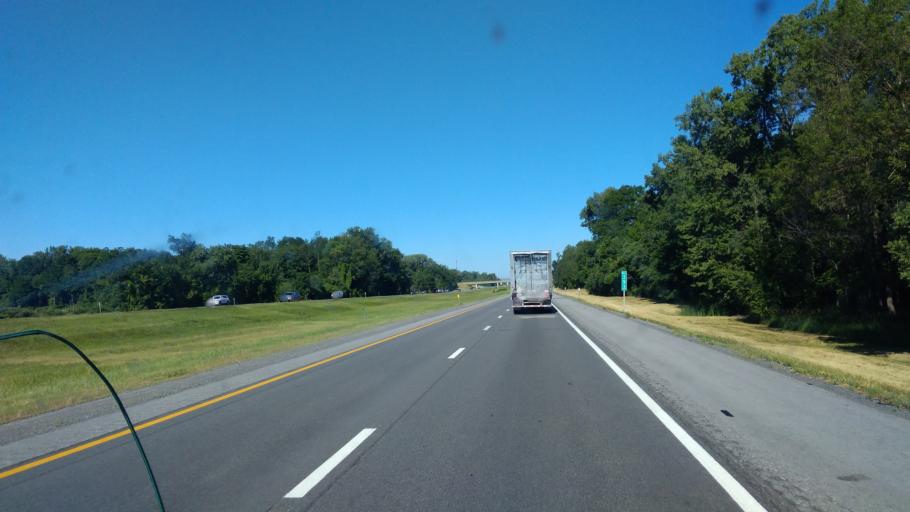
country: US
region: New York
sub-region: Genesee County
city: Oakfield
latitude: 43.0173
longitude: -78.2422
